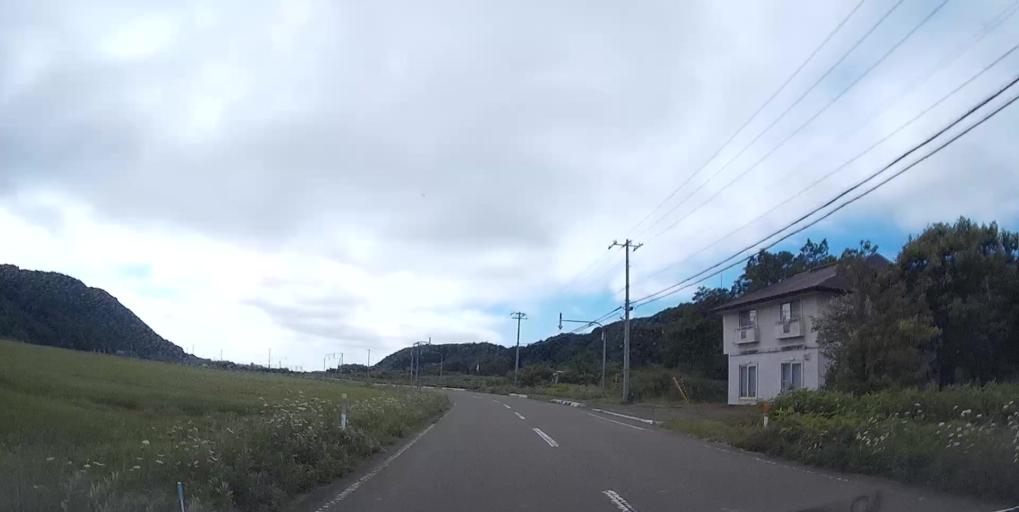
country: JP
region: Hokkaido
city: Kamiiso
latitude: 41.9737
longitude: 140.1607
